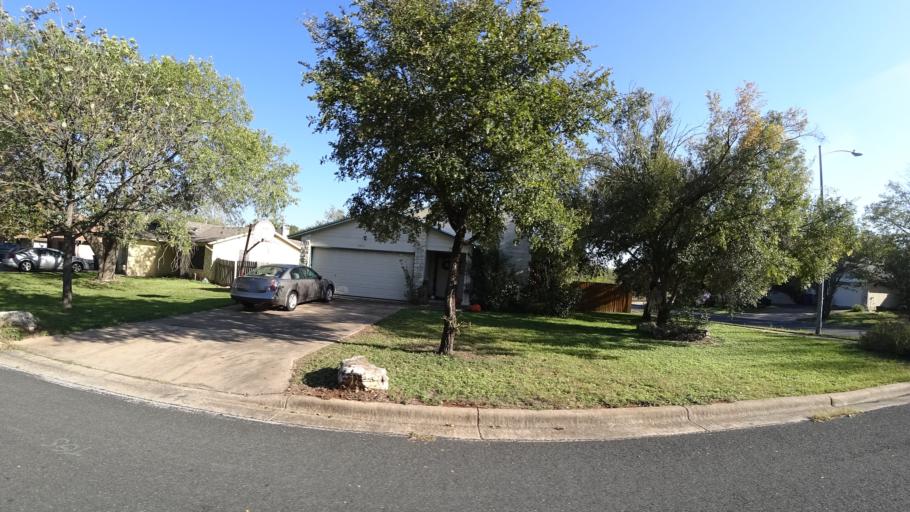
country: US
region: Texas
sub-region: Travis County
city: Shady Hollow
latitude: 30.2061
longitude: -97.8531
